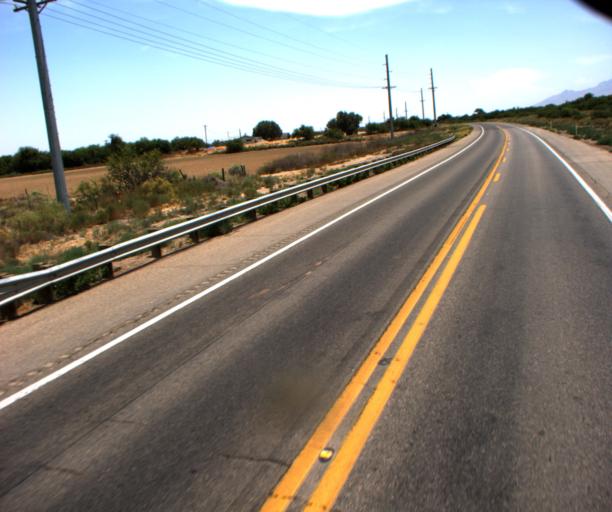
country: US
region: Arizona
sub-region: Graham County
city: Pima
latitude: 32.9449
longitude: -109.9103
